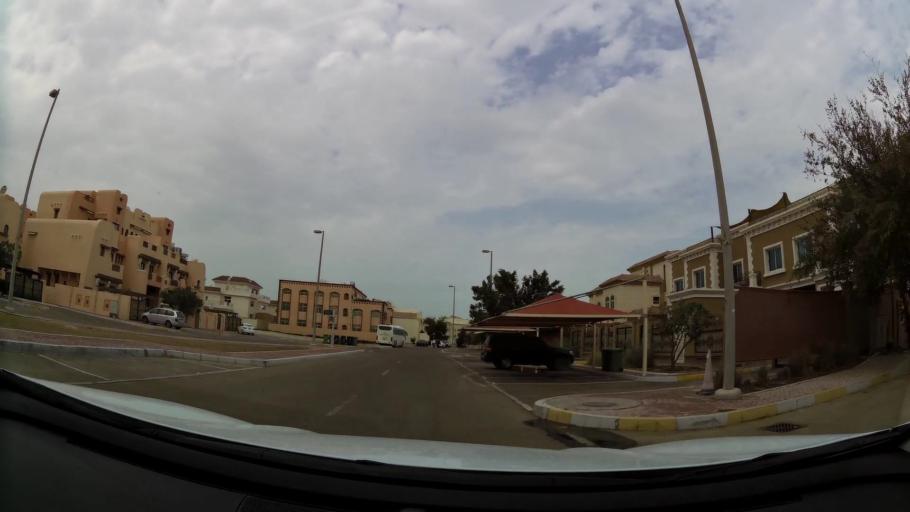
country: AE
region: Abu Dhabi
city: Abu Dhabi
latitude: 24.4309
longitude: 54.4438
